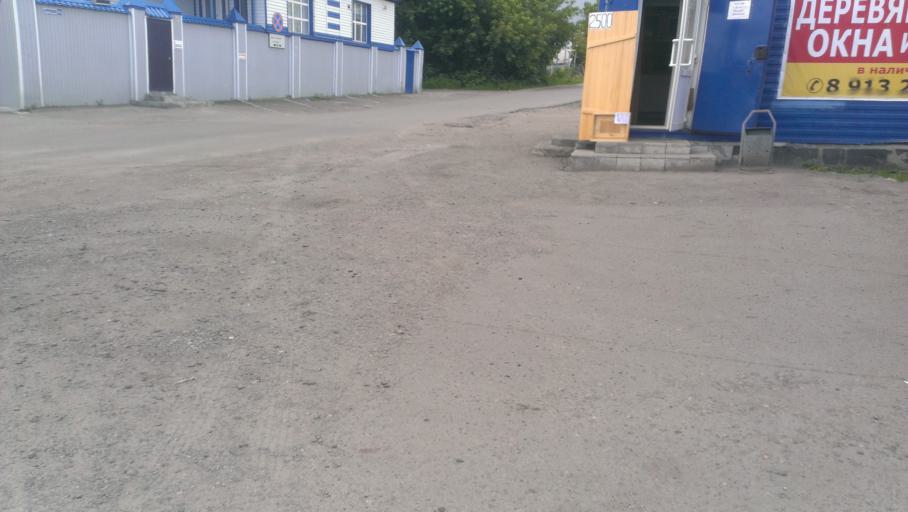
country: RU
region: Altai Krai
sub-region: Gorod Barnaulskiy
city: Barnaul
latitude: 53.3374
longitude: 83.7307
